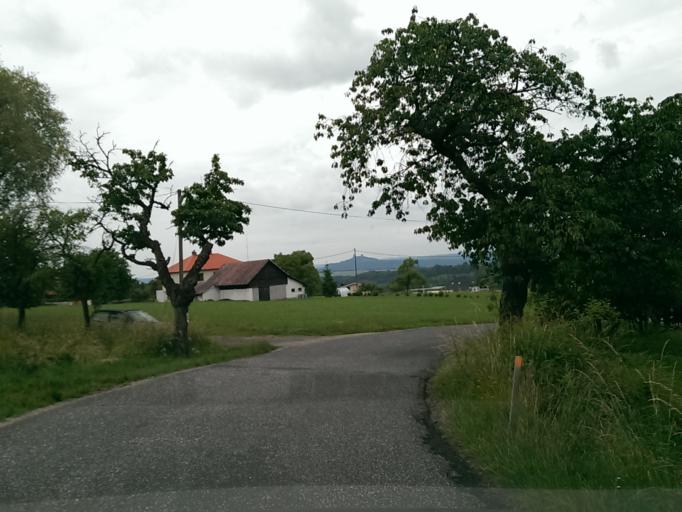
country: CZ
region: Liberecky
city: Rovensko pod Troskami
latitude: 50.5860
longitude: 15.2534
